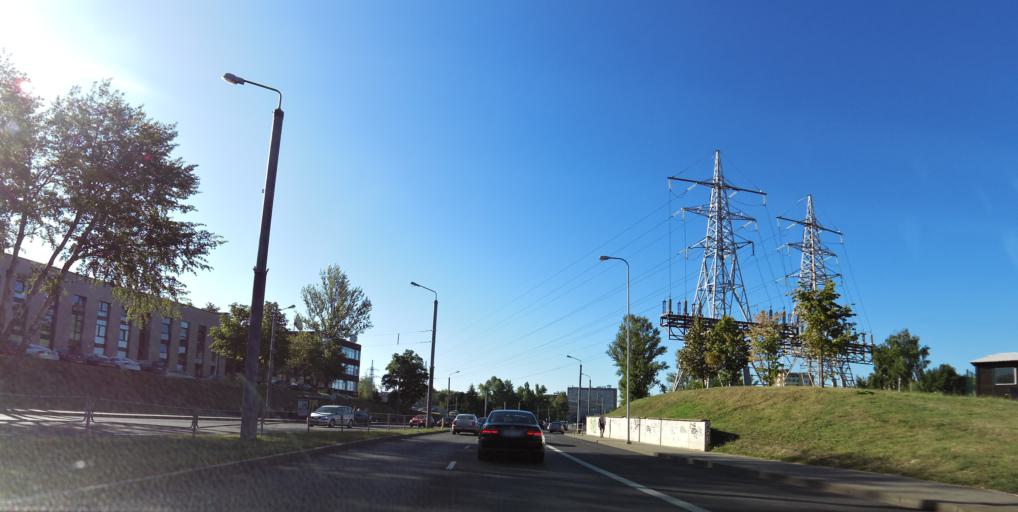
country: LT
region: Vilnius County
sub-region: Vilnius
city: Vilnius
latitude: 54.7168
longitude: 25.2864
